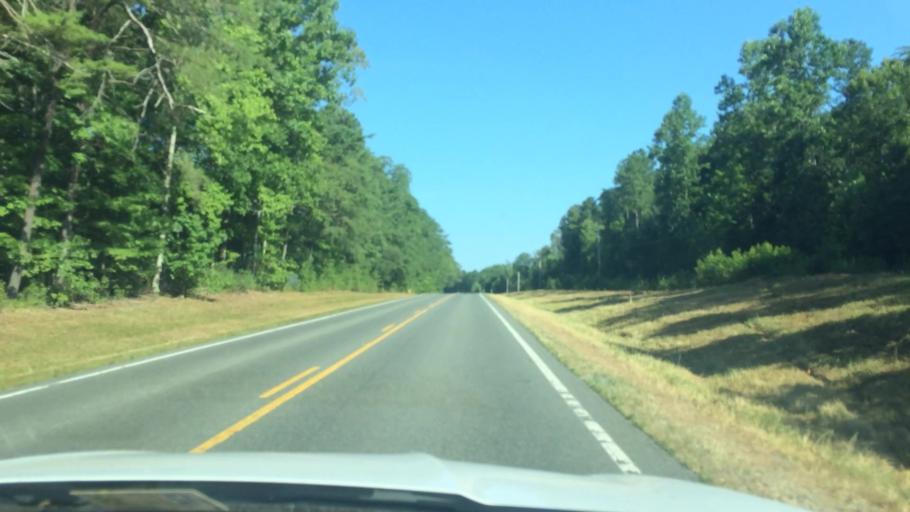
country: US
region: Virginia
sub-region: Lancaster County
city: Lancaster
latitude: 37.8213
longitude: -76.5549
